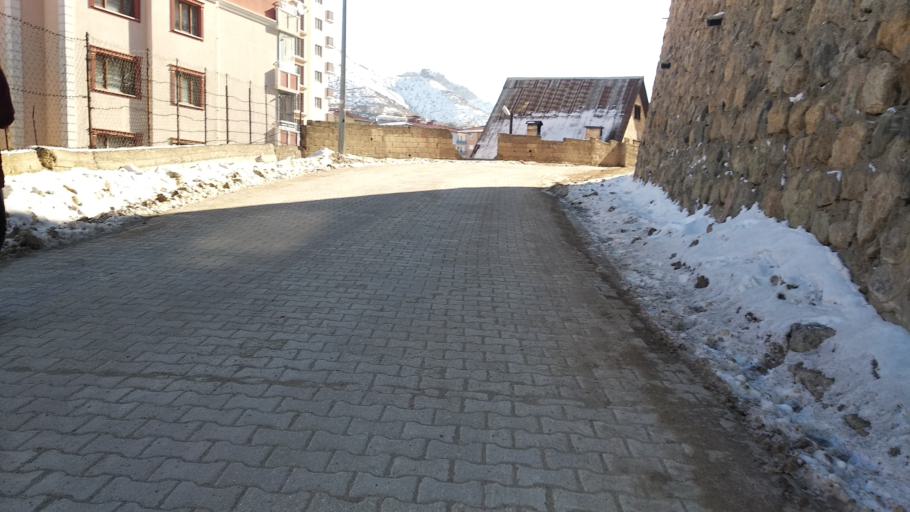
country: TR
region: Gumushane
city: Gumushkhane
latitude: 40.4565
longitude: 39.4866
